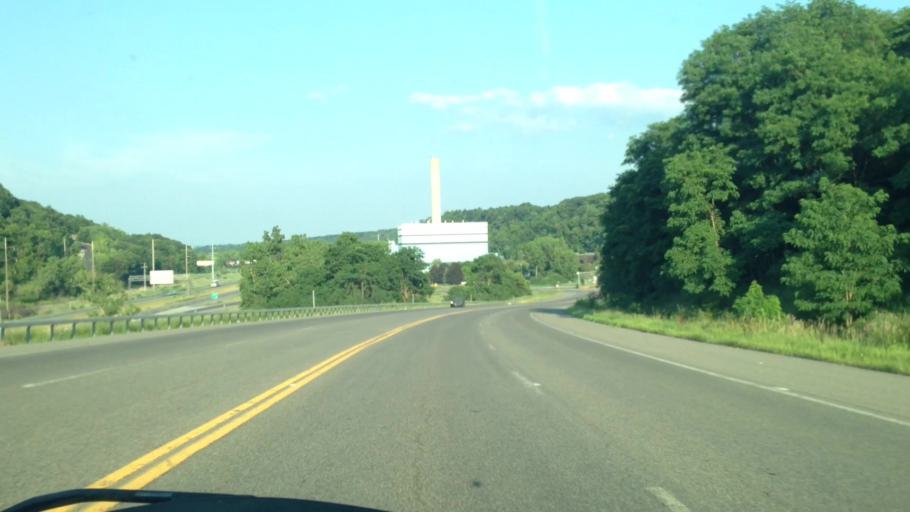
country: US
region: New York
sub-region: Onondaga County
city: Nedrow
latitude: 43.0066
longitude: -76.1229
